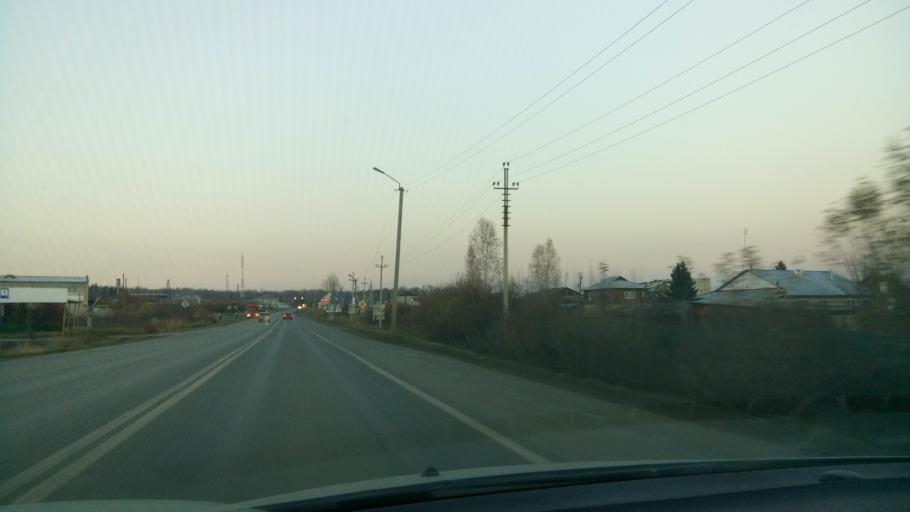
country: RU
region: Sverdlovsk
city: Pyshma
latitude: 56.9475
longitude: 63.2232
